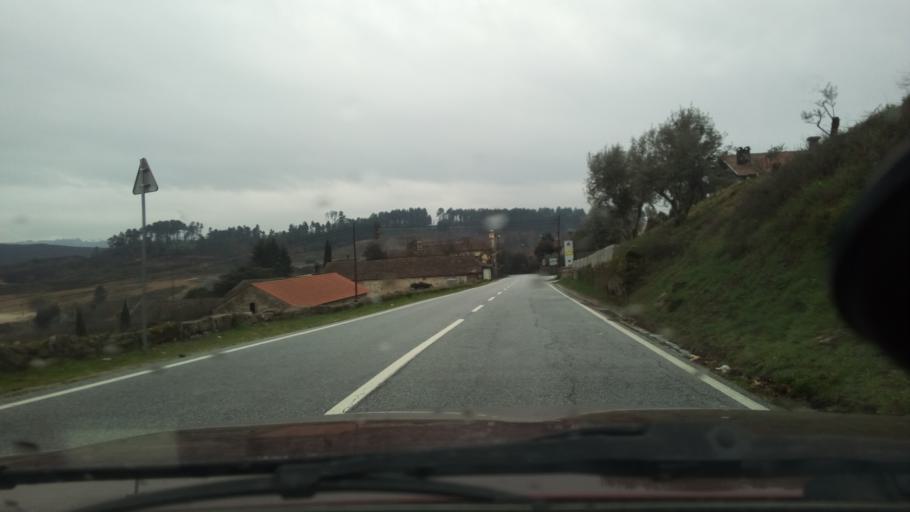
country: PT
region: Viseu
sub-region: Viseu
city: Rio de Loba
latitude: 40.6386
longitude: -7.8369
